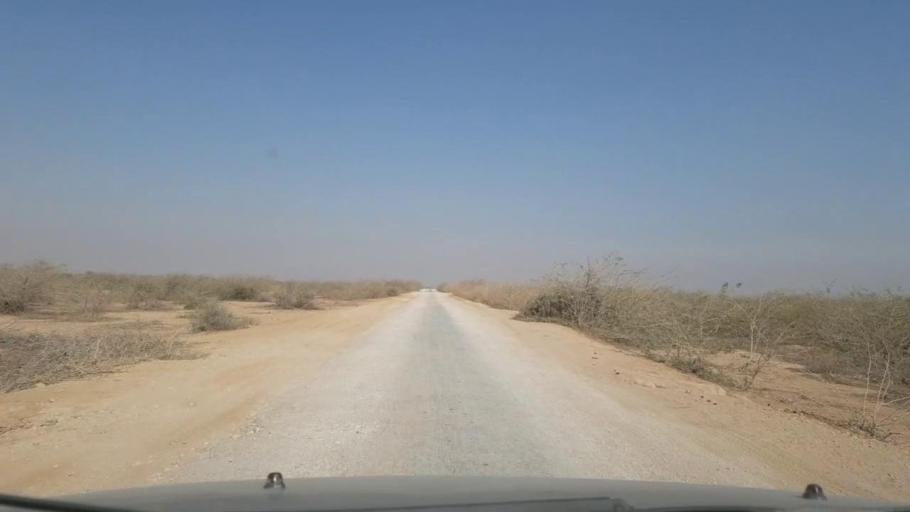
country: PK
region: Sindh
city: Thatta
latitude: 24.9193
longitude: 67.9368
